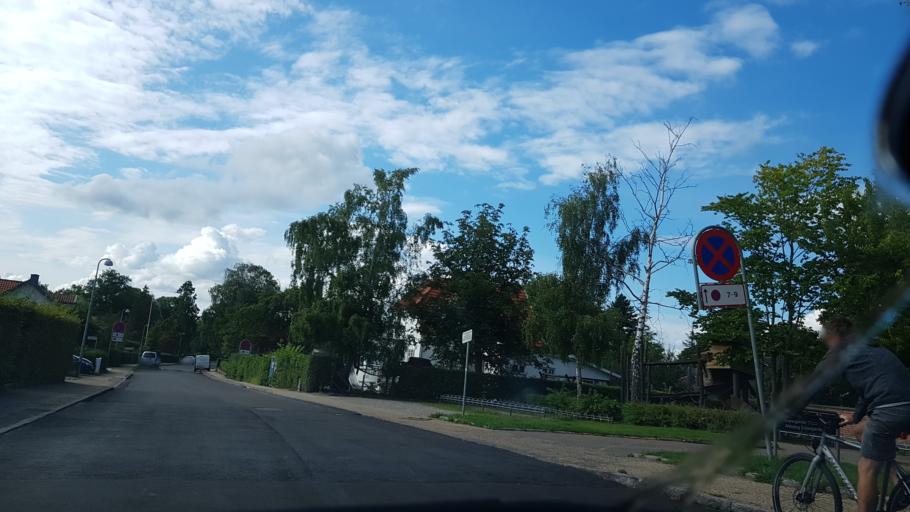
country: DK
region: Capital Region
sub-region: Helsingor Kommune
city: Espergaerde
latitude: 55.9892
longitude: 12.5532
